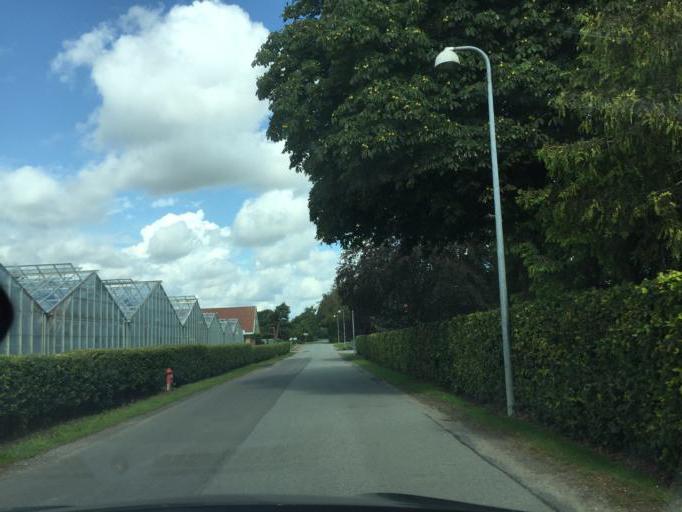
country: DK
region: South Denmark
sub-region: Odense Kommune
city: Stige
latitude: 55.4443
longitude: 10.3907
